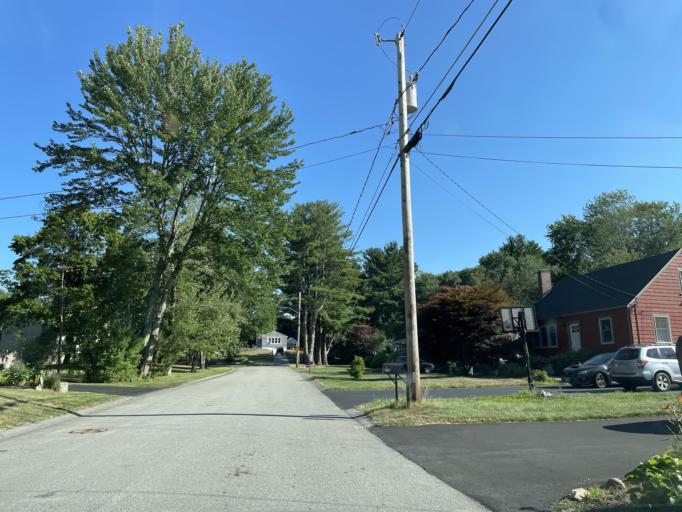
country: US
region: Massachusetts
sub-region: Norfolk County
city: Bellingham
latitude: 42.0955
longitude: -71.4382
